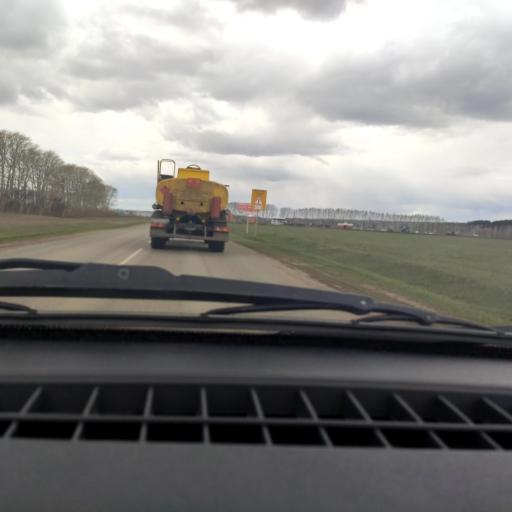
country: RU
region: Bashkortostan
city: Chekmagush
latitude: 55.1286
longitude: 54.6915
